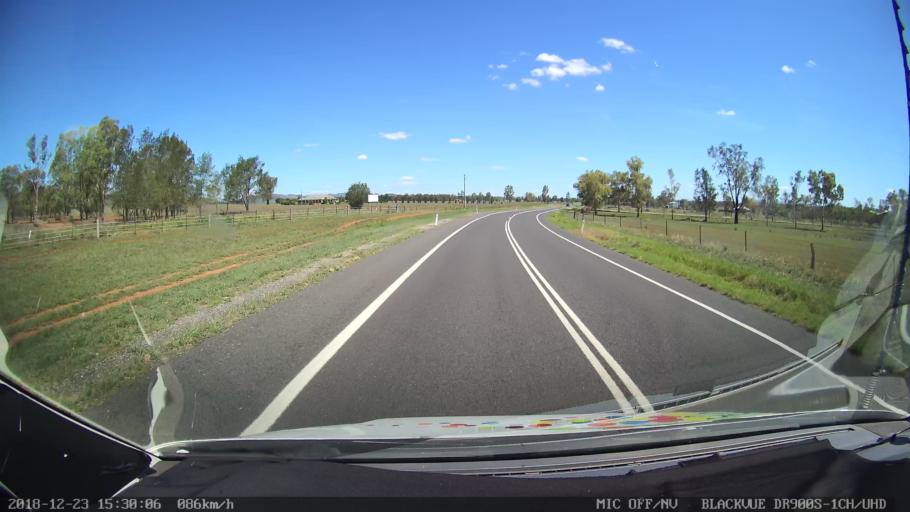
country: AU
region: New South Wales
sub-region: Tamworth Municipality
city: East Tamworth
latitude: -30.9540
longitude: 150.8661
